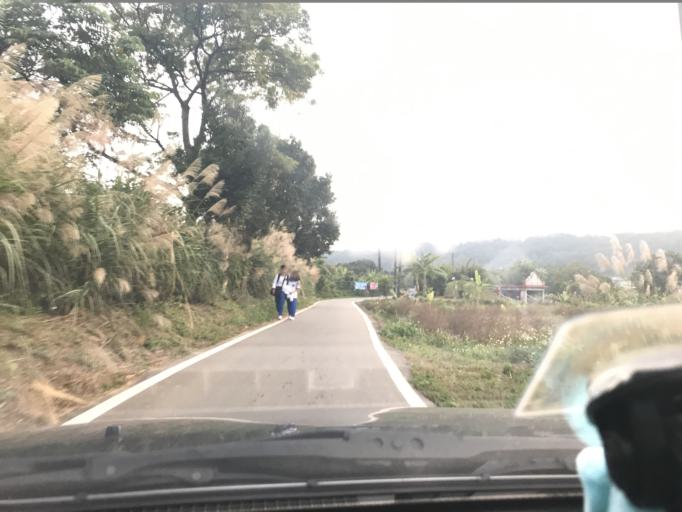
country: TW
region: Taiwan
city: Daxi
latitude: 24.8541
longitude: 121.2112
